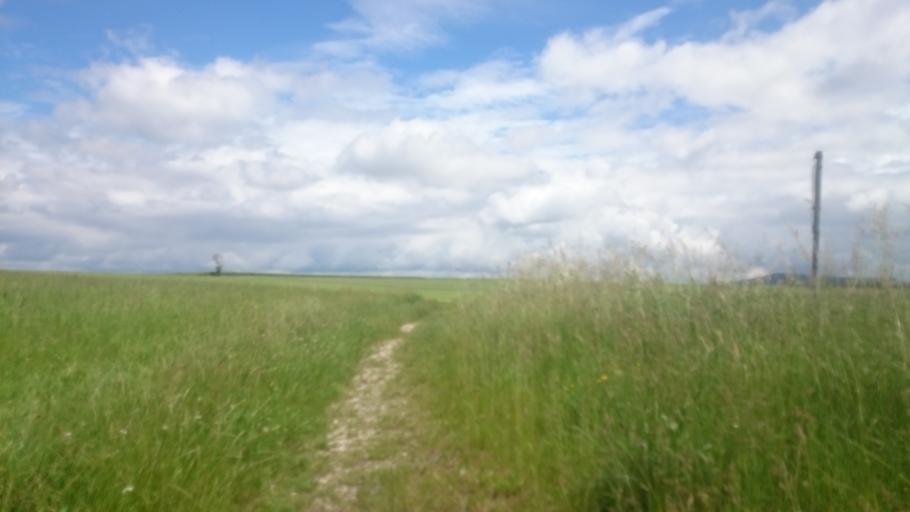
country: DE
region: Bavaria
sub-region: Upper Palatinate
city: Freystadt
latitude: 49.1548
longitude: 11.3108
